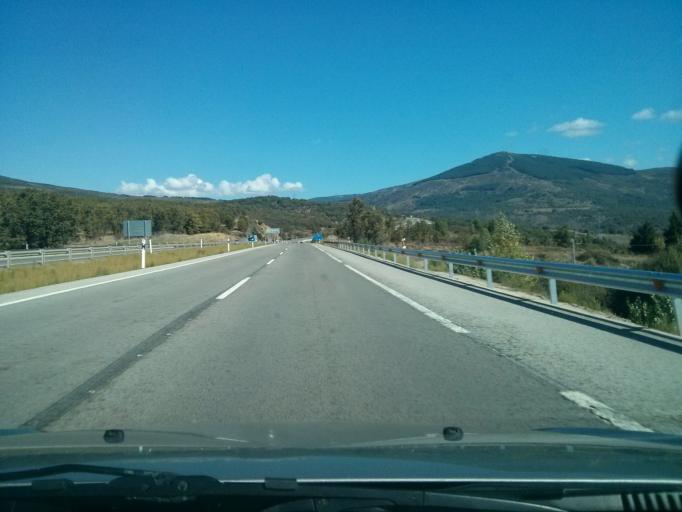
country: ES
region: Madrid
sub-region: Provincia de Madrid
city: Horcajo de la Sierra
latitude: 41.0699
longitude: -3.6062
